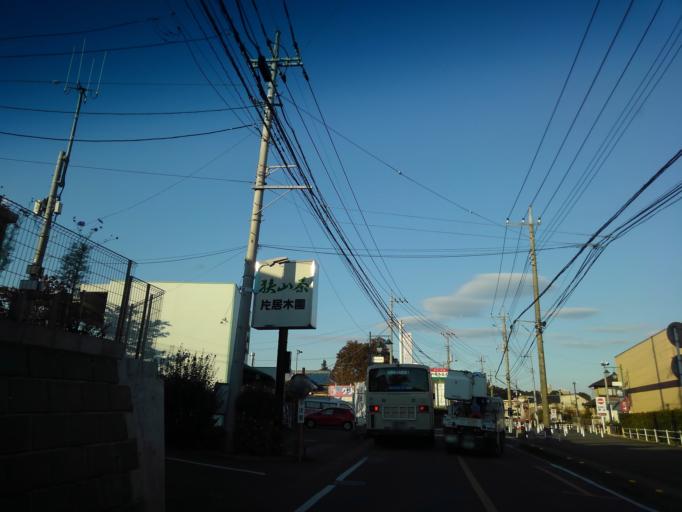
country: JP
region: Saitama
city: Tokorozawa
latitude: 35.7860
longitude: 139.4268
